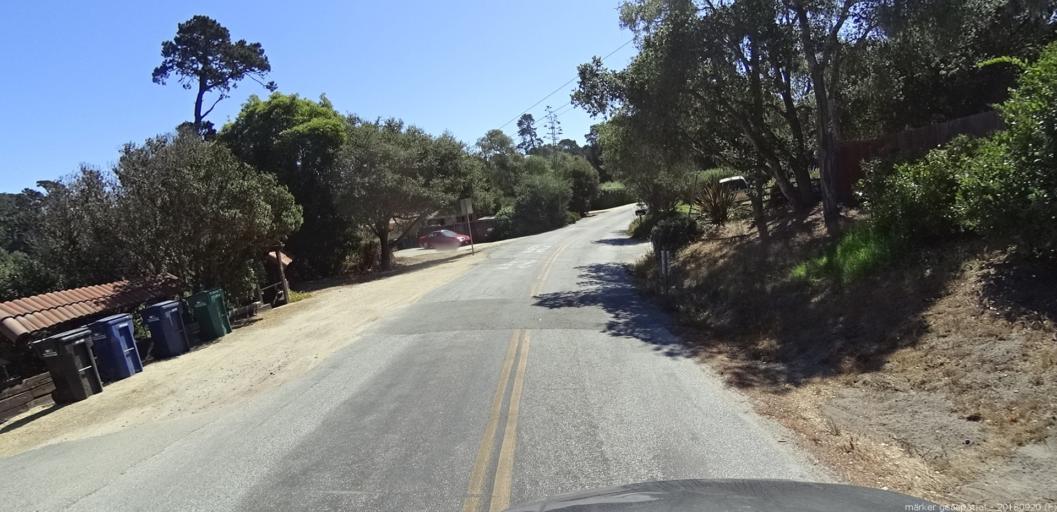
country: US
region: California
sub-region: Monterey County
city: Monterey
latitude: 36.5848
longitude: -121.8681
